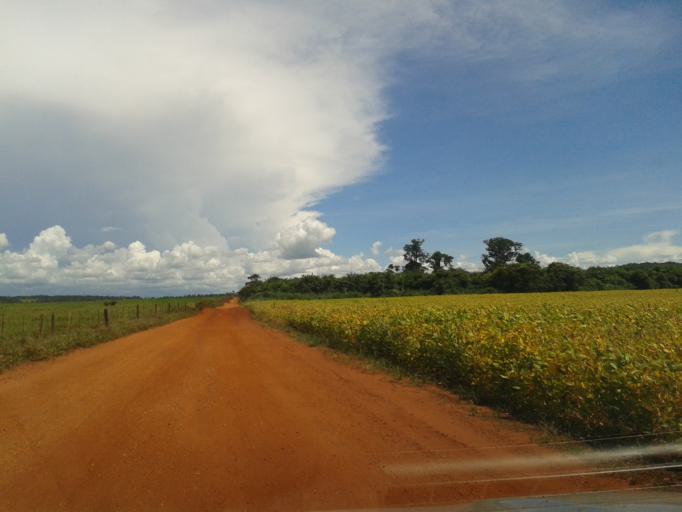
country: BR
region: Minas Gerais
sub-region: Capinopolis
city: Capinopolis
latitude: -18.7040
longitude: -49.7734
